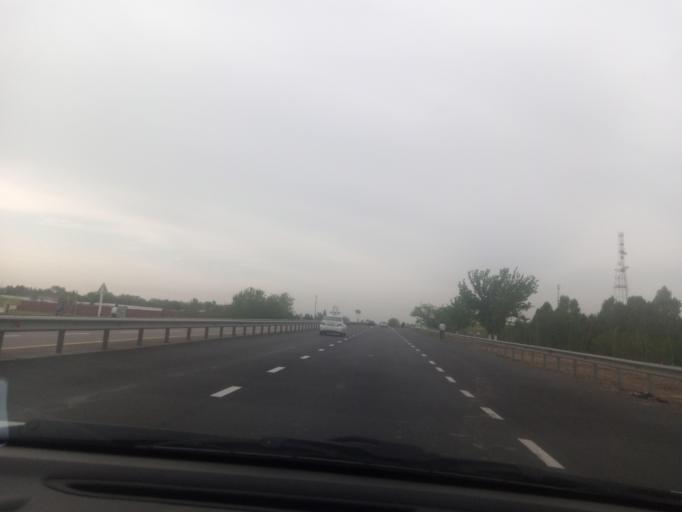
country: UZ
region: Toshkent
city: Tuytepa
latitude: 41.1248
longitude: 69.4387
